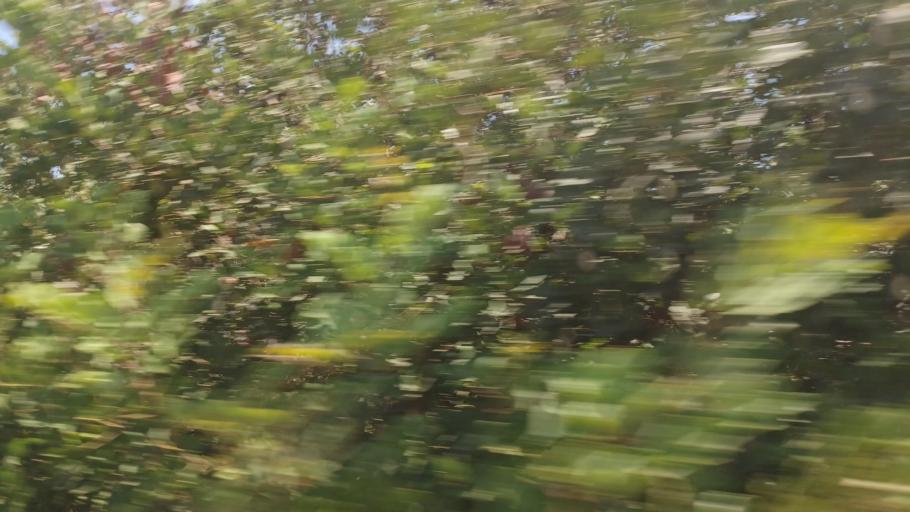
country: CY
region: Pafos
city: Mesogi
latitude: 34.8231
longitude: 32.4589
